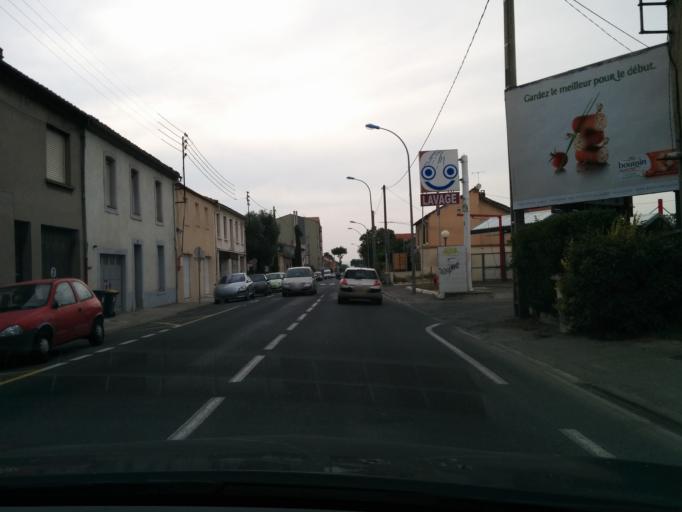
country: FR
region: Languedoc-Roussillon
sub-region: Departement de l'Aude
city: Carcassonne
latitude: 43.2205
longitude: 2.3404
